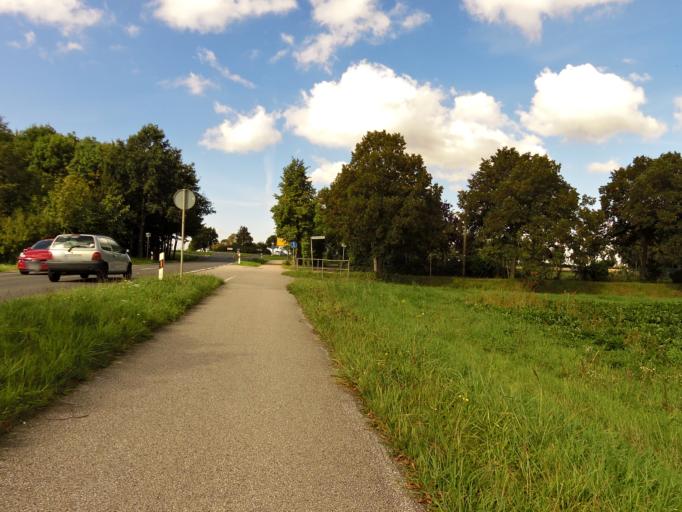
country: DE
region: North Rhine-Westphalia
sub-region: Regierungsbezirk Koln
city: Euskirchen
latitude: 50.6419
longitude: 6.8425
